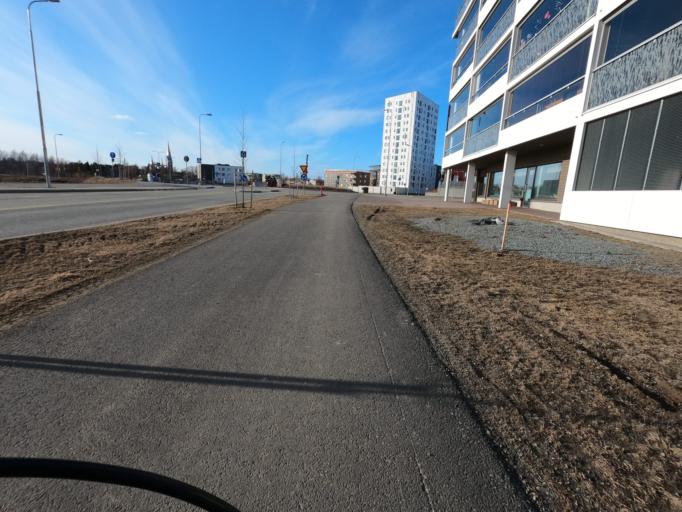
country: FI
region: North Karelia
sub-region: Joensuu
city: Joensuu
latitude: 62.5910
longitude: 29.7599
